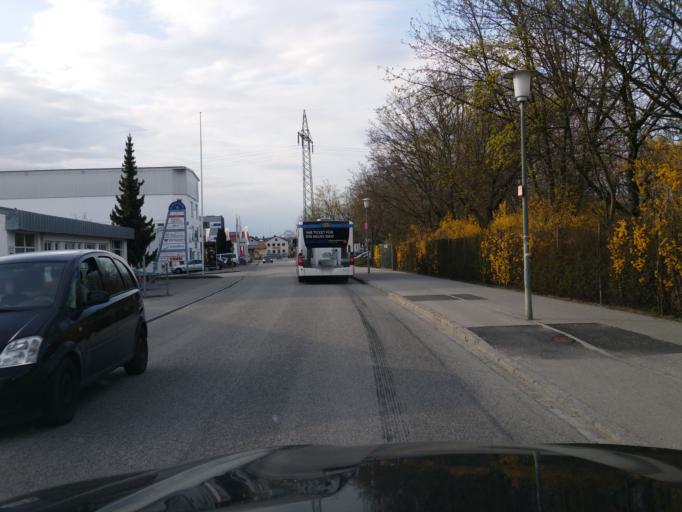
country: DE
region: Bavaria
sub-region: Lower Bavaria
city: Ergolding
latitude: 48.5629
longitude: 12.1672
